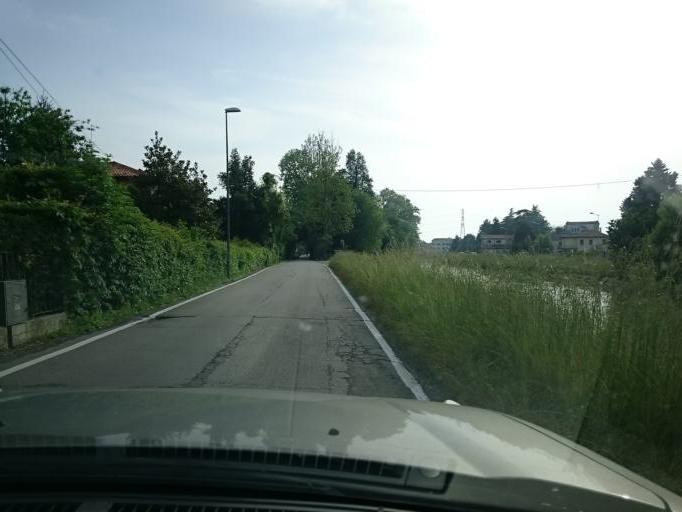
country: IT
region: Veneto
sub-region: Provincia di Venezia
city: Mira Taglio
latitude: 45.4320
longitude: 12.1146
